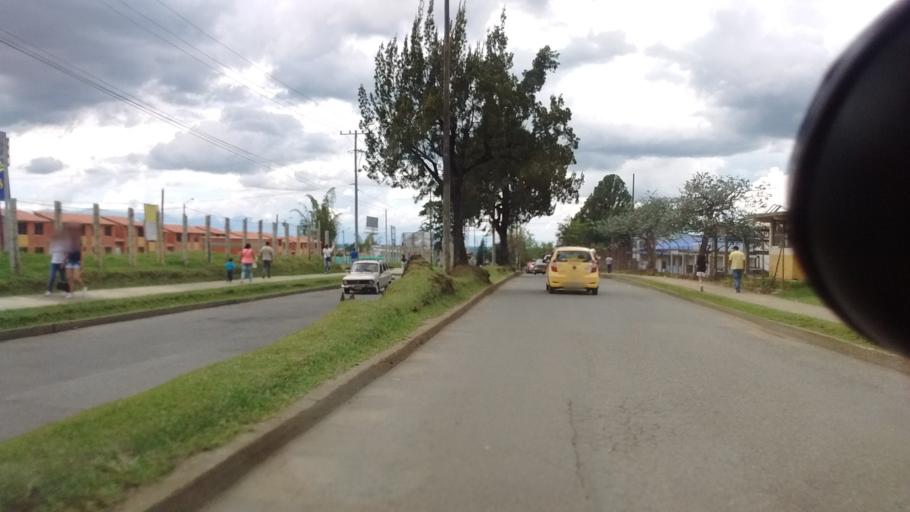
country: CO
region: Cauca
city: Popayan
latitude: 2.4808
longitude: -76.5620
